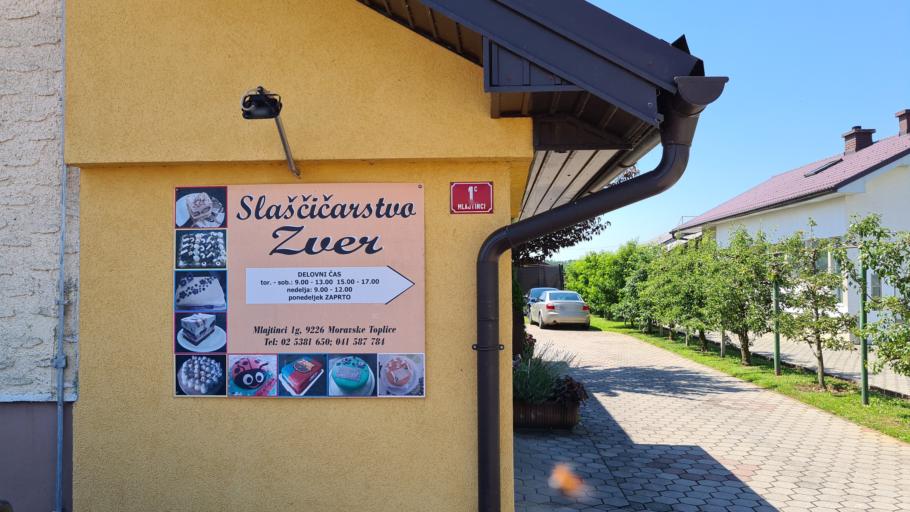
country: SI
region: Moravske Toplice
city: Moravske Toplice
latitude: 46.6695
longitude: 16.2192
